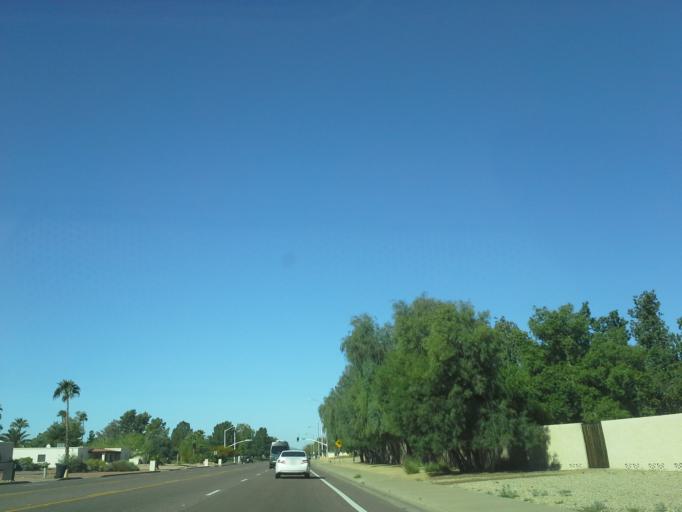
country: US
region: Arizona
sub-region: Maricopa County
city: Paradise Valley
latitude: 33.5966
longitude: -111.8976
